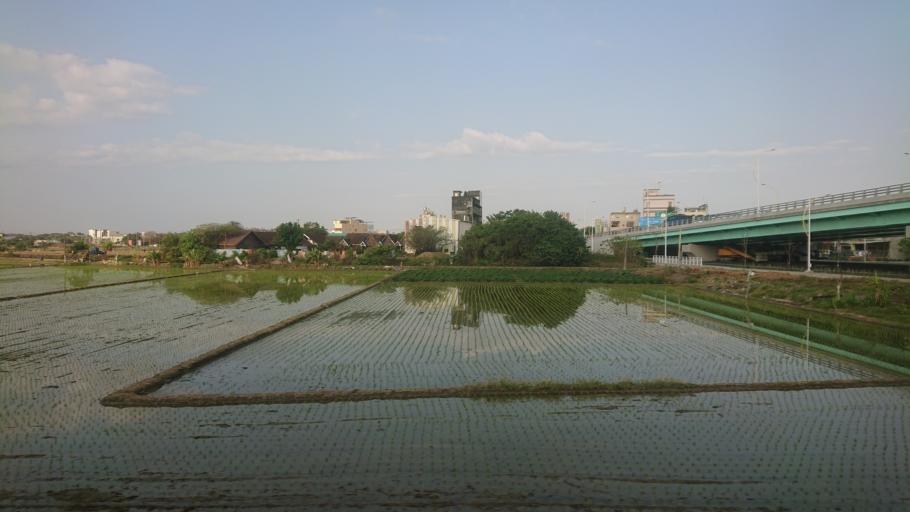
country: TW
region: Taiwan
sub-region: Chiayi
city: Jiayi Shi
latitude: 23.5489
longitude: 120.4298
